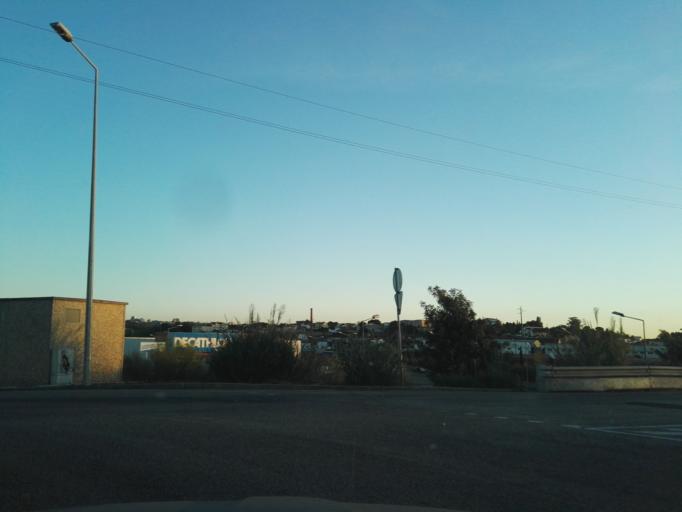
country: PT
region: Santarem
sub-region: Santarem
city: Santarem
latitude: 39.2606
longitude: -8.7032
